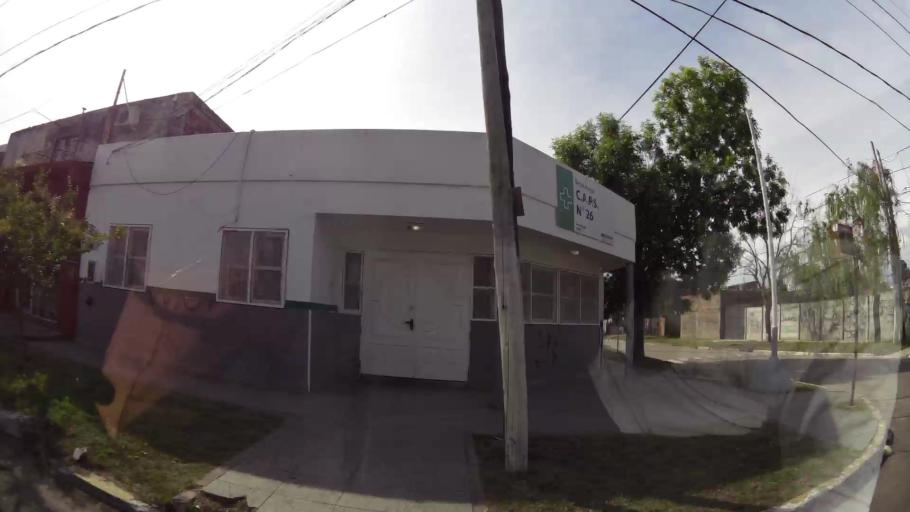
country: AR
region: Buenos Aires
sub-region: Partido de Quilmes
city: Quilmes
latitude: -34.7686
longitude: -58.2484
